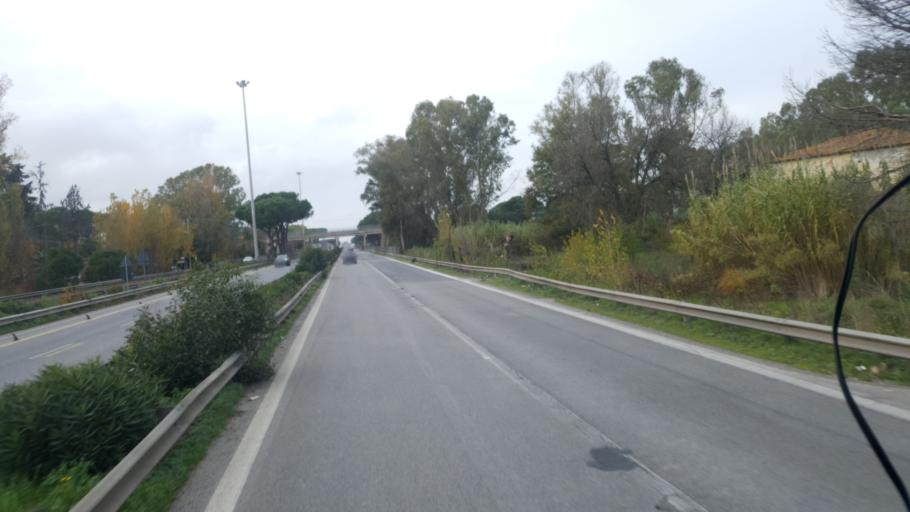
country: IT
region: Latium
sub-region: Provincia di Latina
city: Borgo Podgora
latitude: 41.4875
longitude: 12.8487
